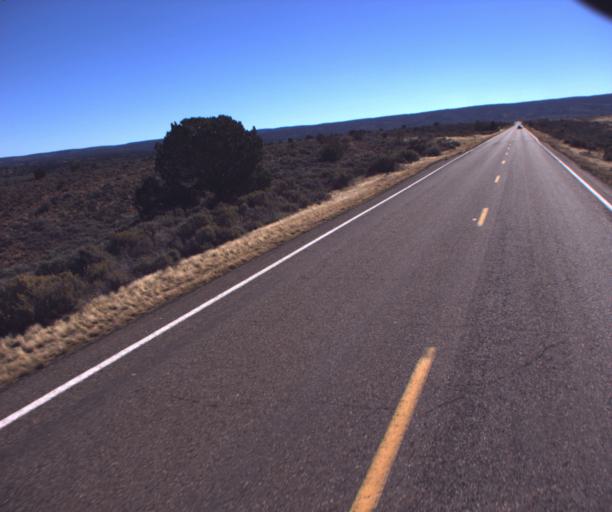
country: US
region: Arizona
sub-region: Coconino County
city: Fredonia
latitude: 36.8677
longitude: -112.3208
